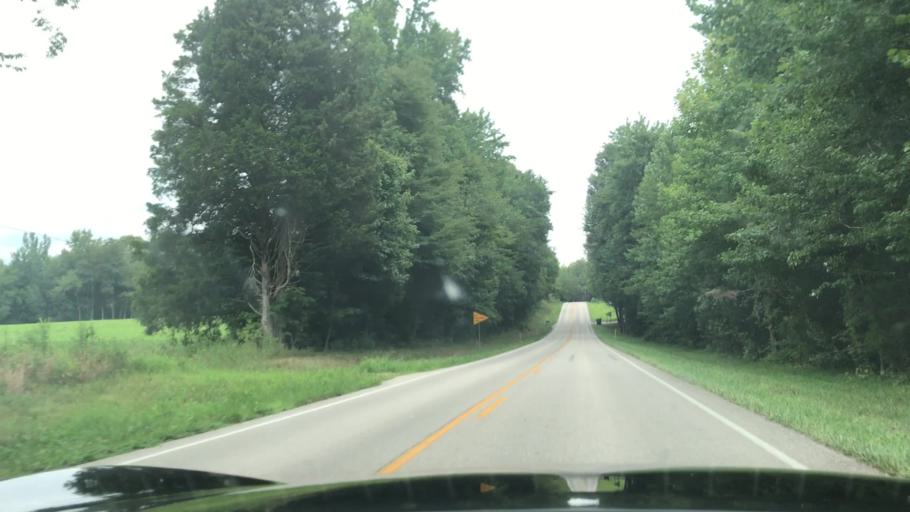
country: US
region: Kentucky
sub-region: Butler County
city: Morgantown
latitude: 37.1796
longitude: -86.7958
